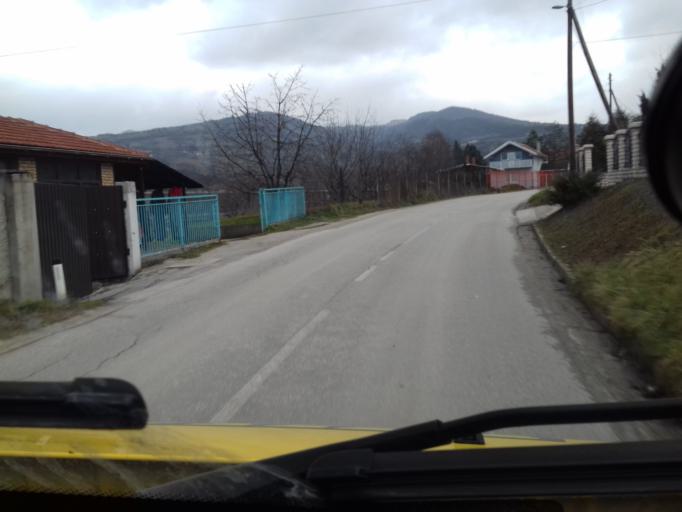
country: BA
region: Federation of Bosnia and Herzegovina
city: Zenica
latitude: 44.1802
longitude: 17.9649
